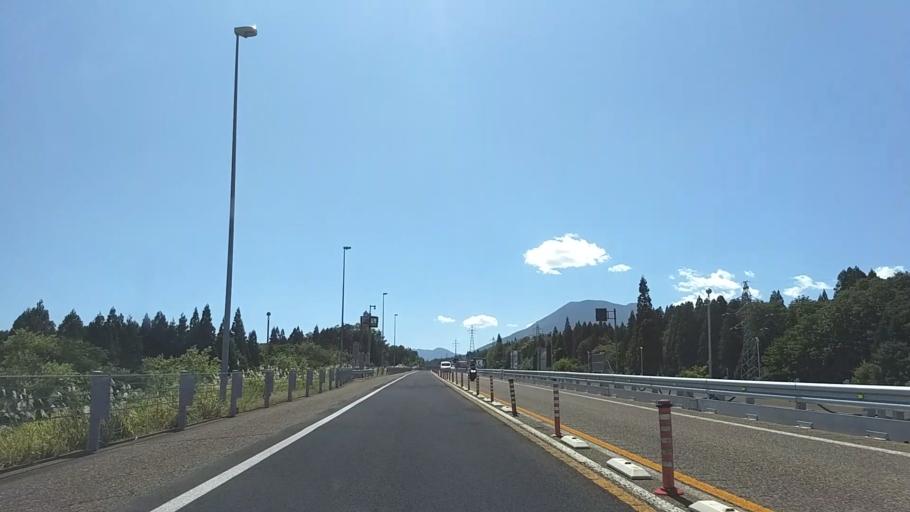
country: JP
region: Niigata
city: Arai
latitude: 36.8955
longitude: 138.2056
